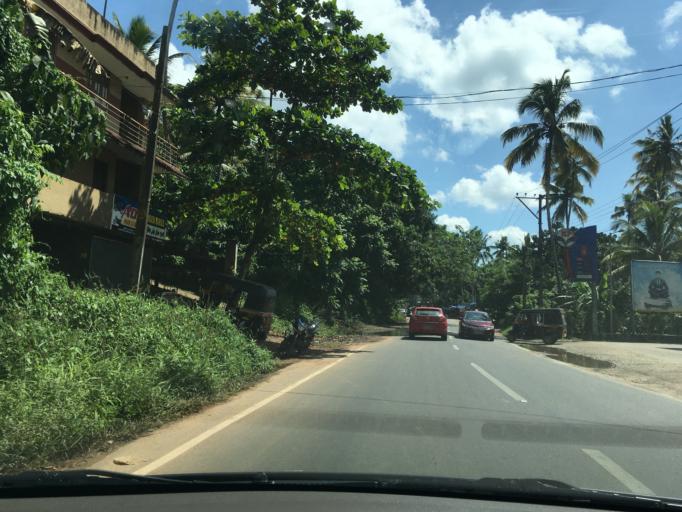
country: IN
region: Kerala
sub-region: Thiruvananthapuram
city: Nedumangad
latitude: 8.5926
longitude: 76.9951
